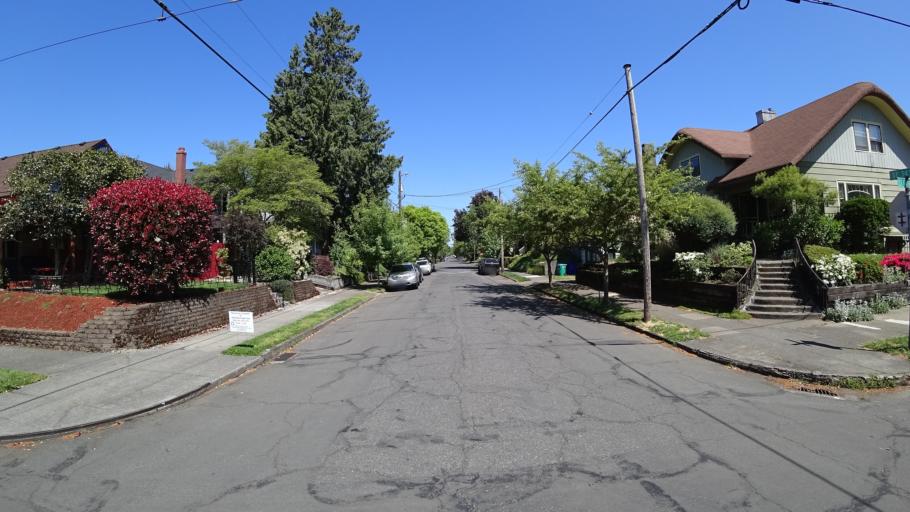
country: US
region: Oregon
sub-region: Multnomah County
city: Portland
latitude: 45.5074
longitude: -122.6296
